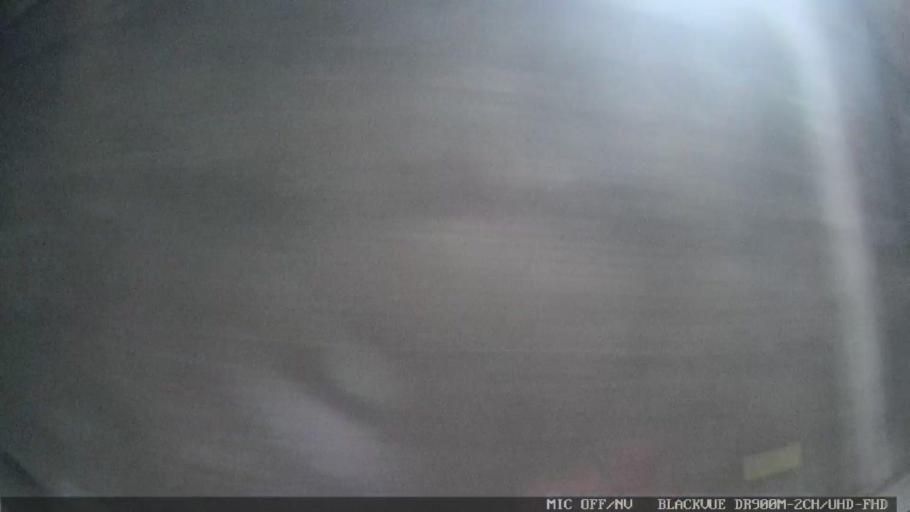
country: BR
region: Sao Paulo
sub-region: Cubatao
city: Cubatao
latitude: -23.8796
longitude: -46.4836
